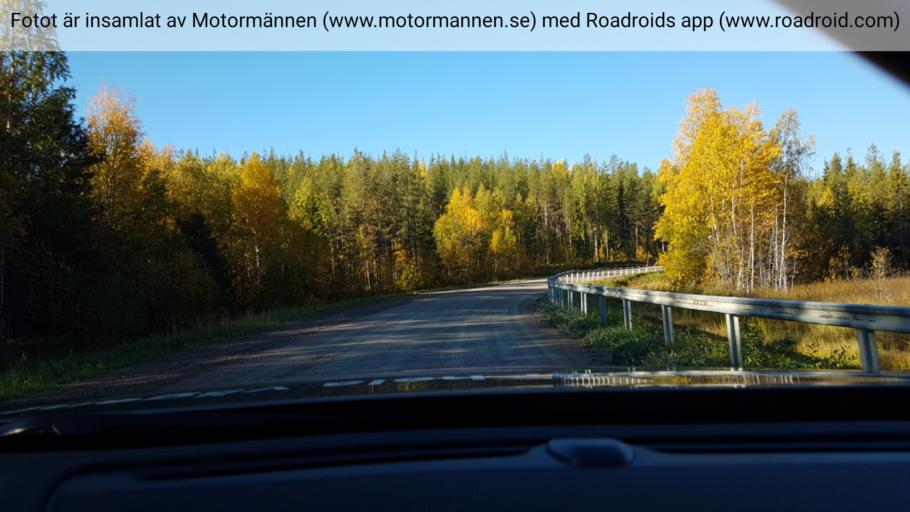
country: SE
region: Norrbotten
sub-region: Alvsbyns Kommun
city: AElvsbyn
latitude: 66.2640
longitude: 21.0750
